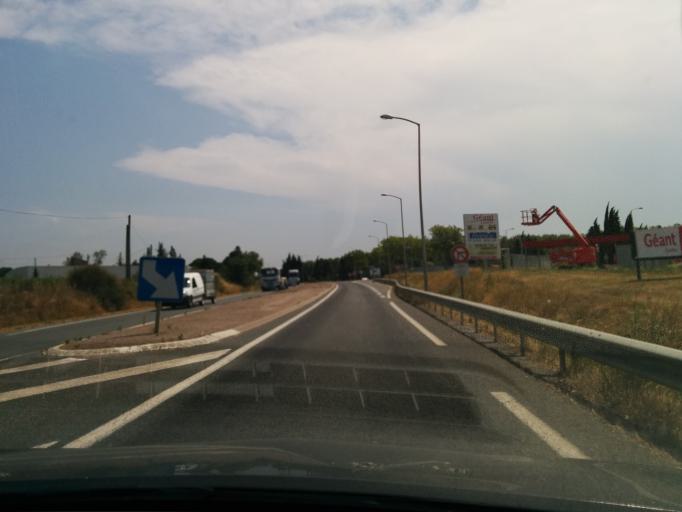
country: FR
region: Languedoc-Roussillon
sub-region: Departement de l'Aude
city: Castelnaudary
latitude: 43.3110
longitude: 1.9719
